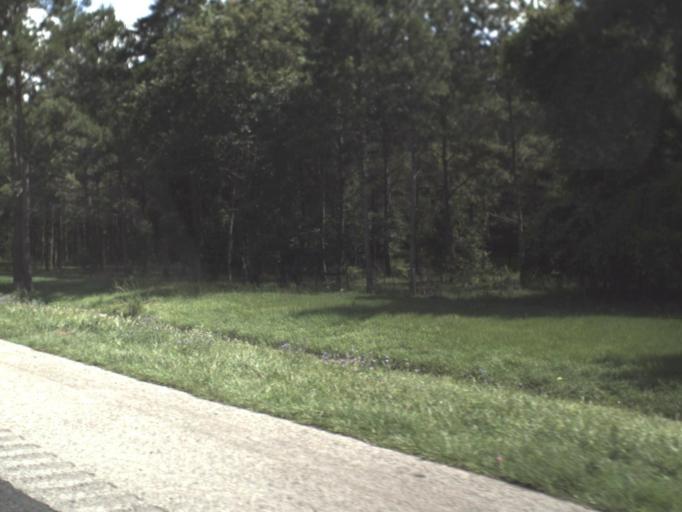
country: US
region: Florida
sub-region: Alachua County
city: Alachua
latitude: 29.7288
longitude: -82.4725
